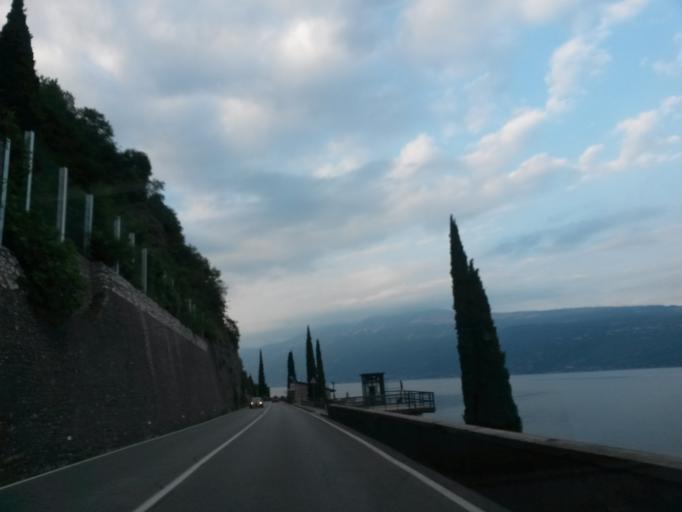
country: IT
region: Lombardy
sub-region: Provincia di Brescia
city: Toscolano Maderno
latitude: 45.6471
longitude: 10.6198
